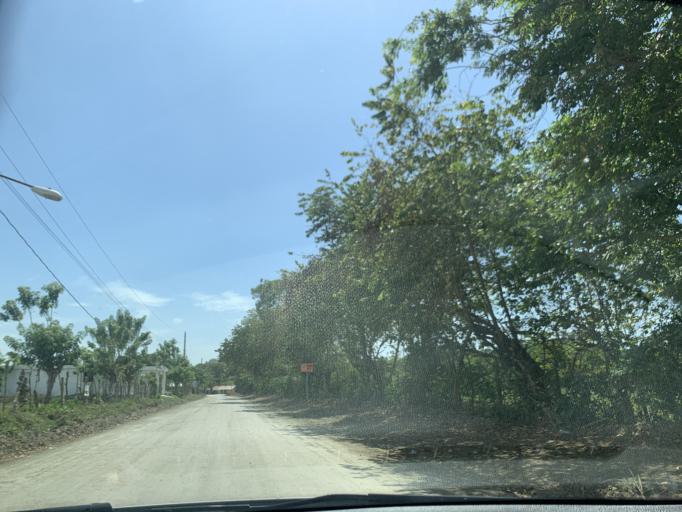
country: DO
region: Puerto Plata
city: Luperon
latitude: 19.8826
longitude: -70.8353
